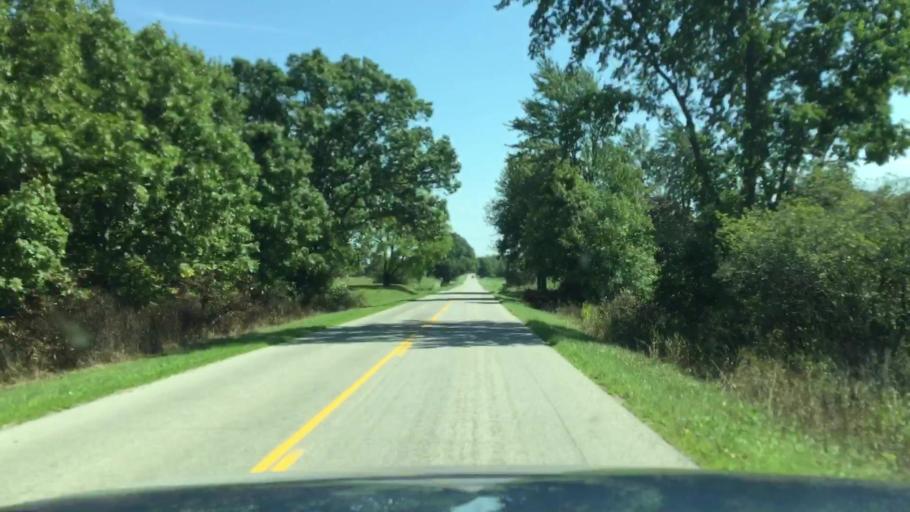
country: US
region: Michigan
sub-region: Lenawee County
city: Clinton
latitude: 42.0655
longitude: -83.9334
